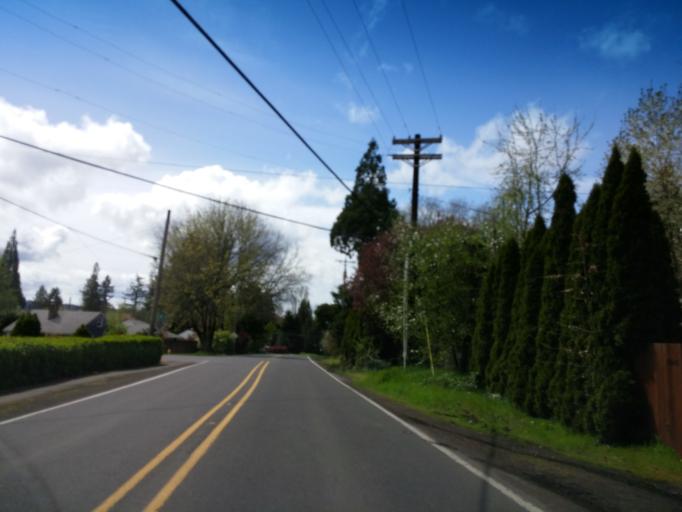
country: US
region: Oregon
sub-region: Washington County
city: Cedar Hills
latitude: 45.5004
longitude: -122.7985
